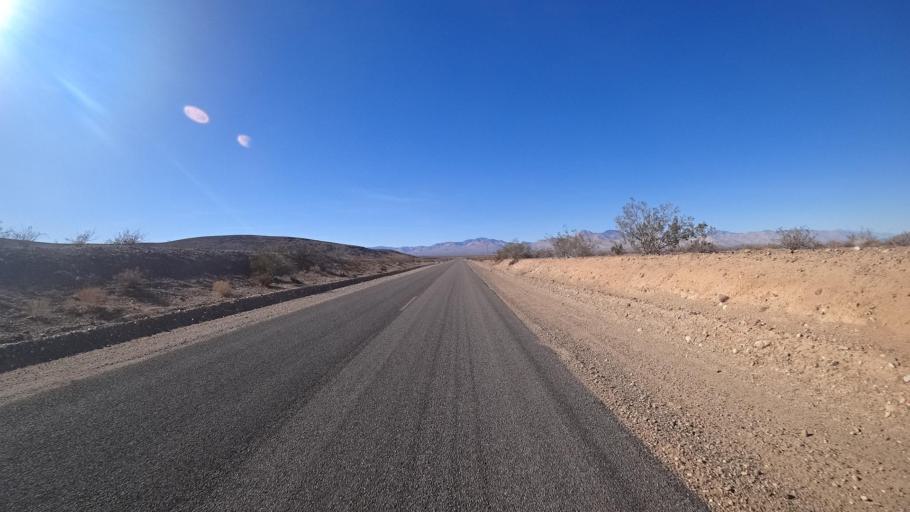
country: US
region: California
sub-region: Kern County
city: China Lake Acres
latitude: 35.5572
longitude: -117.7510
